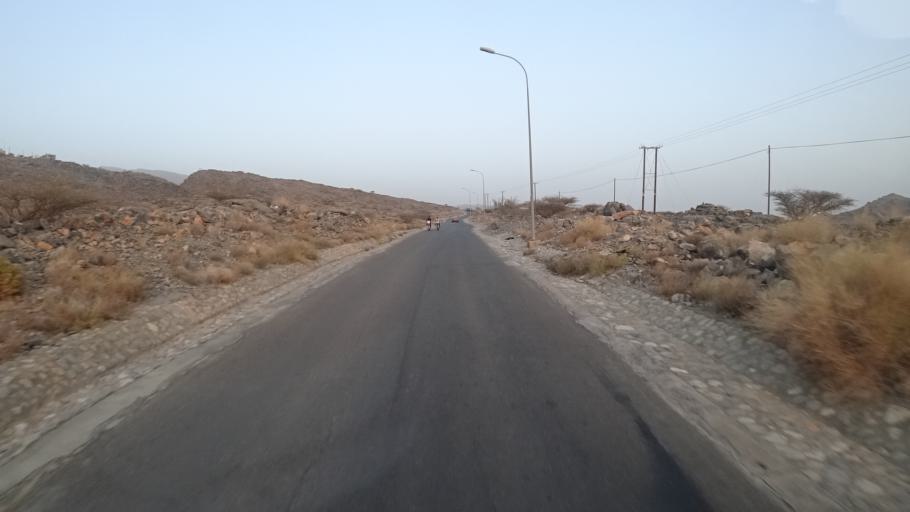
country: OM
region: Muhafazat ad Dakhiliyah
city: Bahla'
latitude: 23.1292
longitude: 57.3024
